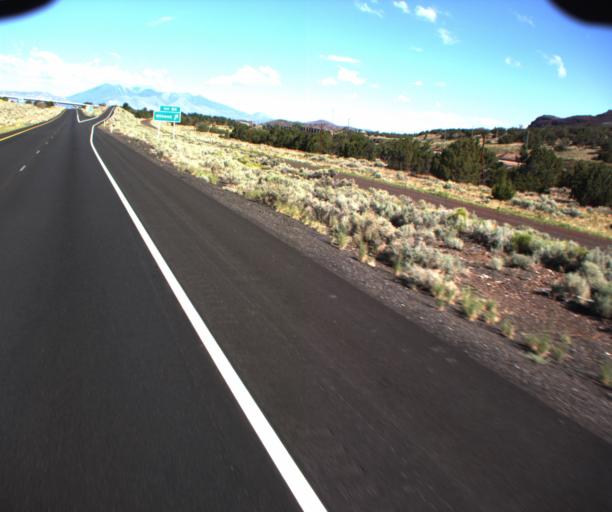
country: US
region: Arizona
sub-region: Coconino County
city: Flagstaff
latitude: 35.1992
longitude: -111.4002
